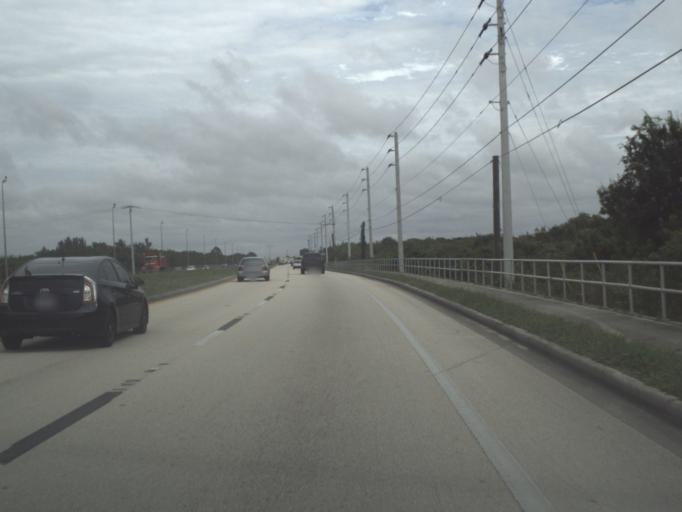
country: US
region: Florida
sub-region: Sarasota County
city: North Port
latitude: 26.9487
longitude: -82.2148
